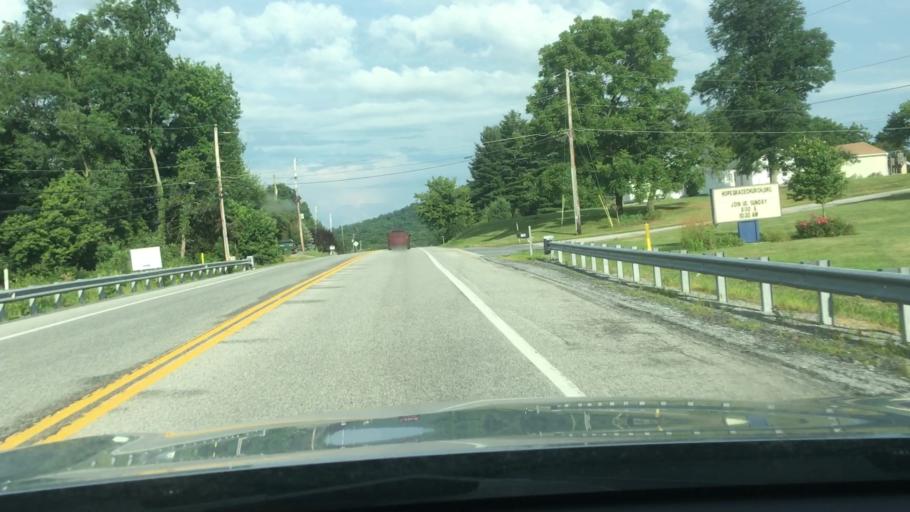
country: US
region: Pennsylvania
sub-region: York County
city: Dillsburg
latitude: 40.1041
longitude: -77.0154
